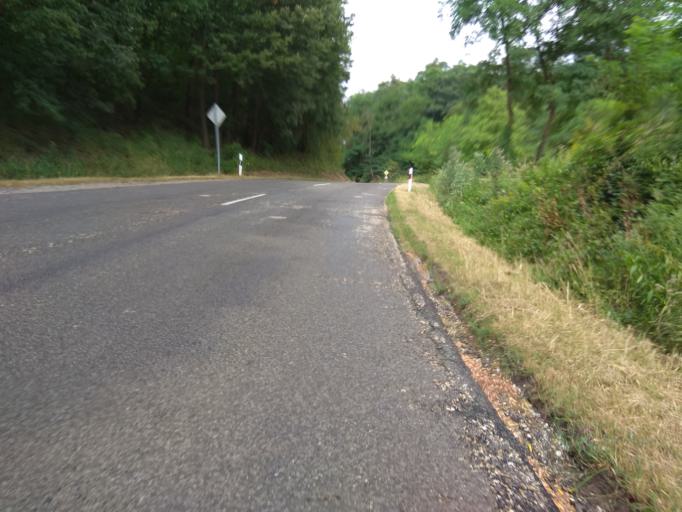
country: HU
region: Heves
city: Tarnalelesz
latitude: 48.0552
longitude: 20.2245
